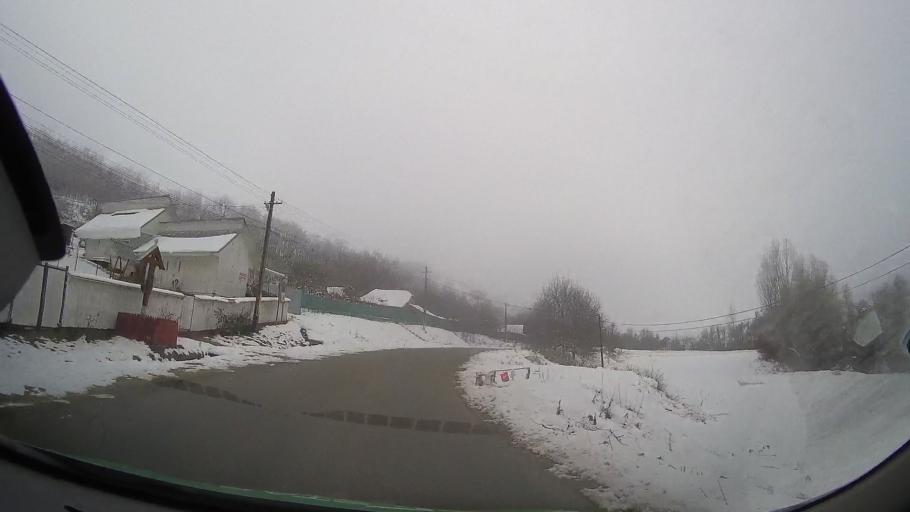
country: RO
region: Bacau
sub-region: Comuna Vultureni
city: Vultureni
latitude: 46.3913
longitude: 27.2795
